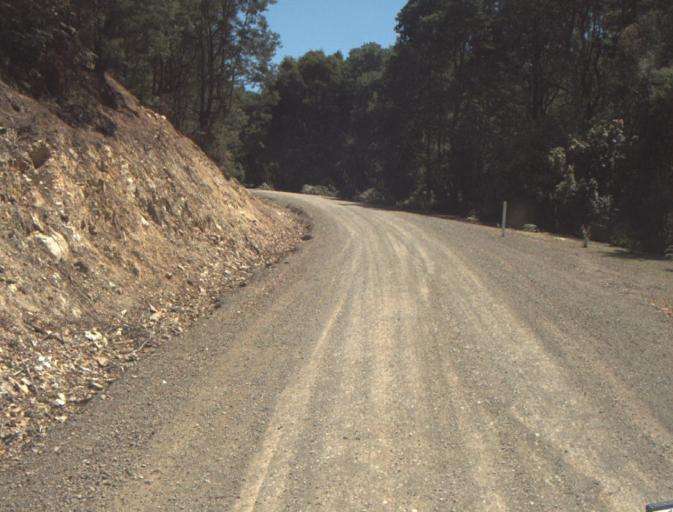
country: AU
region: Tasmania
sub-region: Dorset
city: Scottsdale
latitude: -41.2989
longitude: 147.3587
